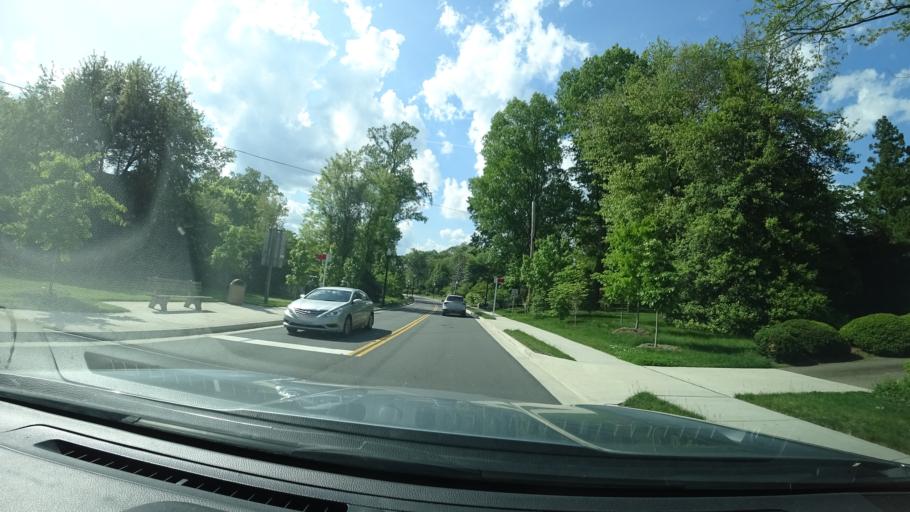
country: US
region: Maryland
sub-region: Montgomery County
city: Brookmont
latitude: 38.9078
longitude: -77.1328
